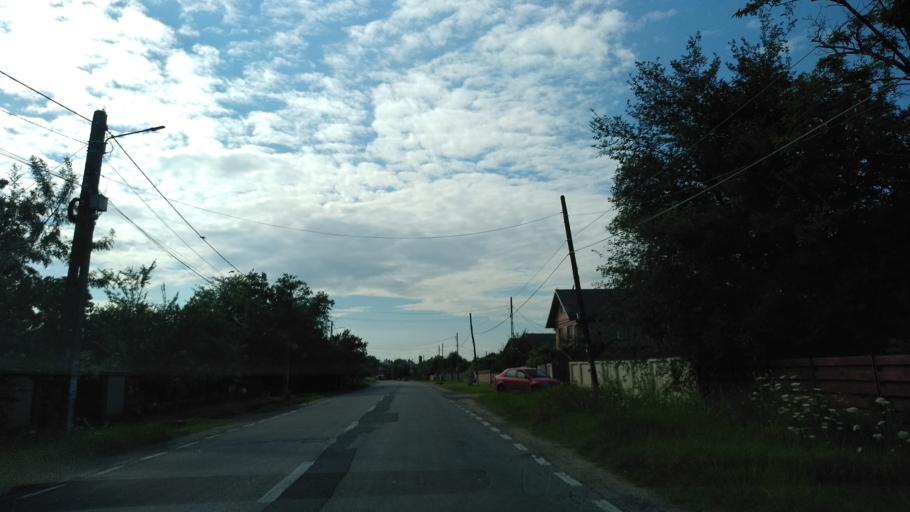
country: RO
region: Dambovita
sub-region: Comuna Petresti
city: Petresti
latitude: 44.6447
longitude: 25.3435
